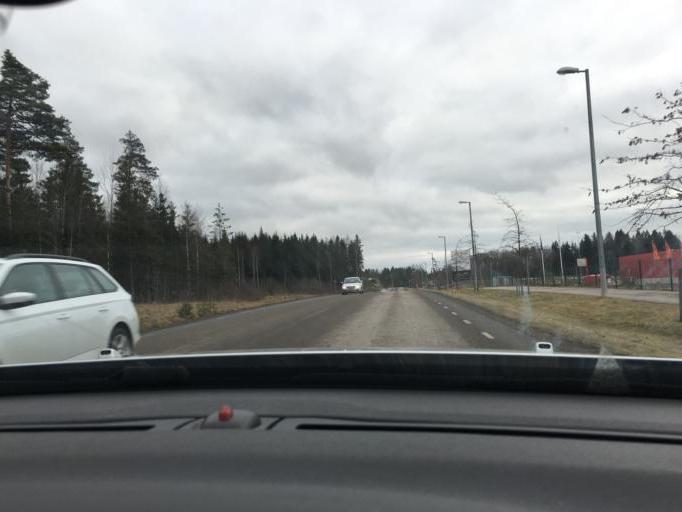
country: SE
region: Soedermanland
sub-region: Katrineholms Kommun
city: Katrineholm
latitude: 58.9980
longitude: 16.2405
